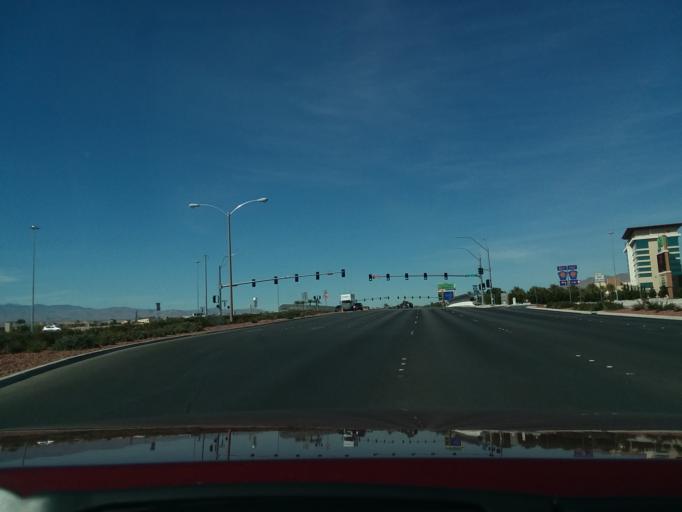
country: US
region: Nevada
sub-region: Clark County
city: North Las Vegas
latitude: 36.2887
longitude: -115.1787
